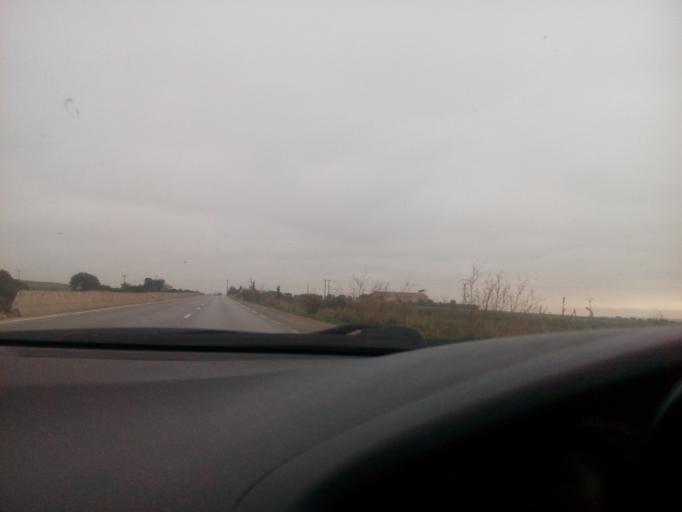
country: DZ
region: Oran
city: Bou Tlelis
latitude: 35.5551
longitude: -0.9424
